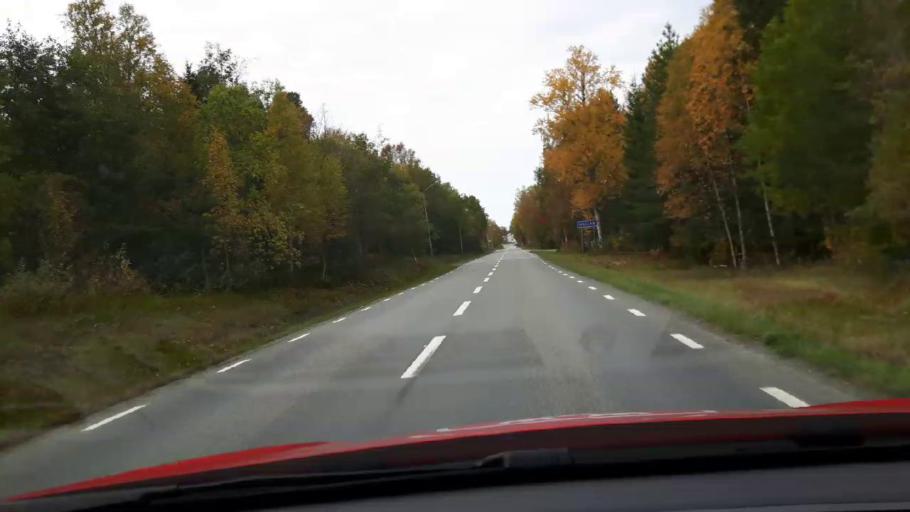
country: SE
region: Jaemtland
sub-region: Krokoms Kommun
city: Krokom
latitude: 63.1705
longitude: 14.1053
